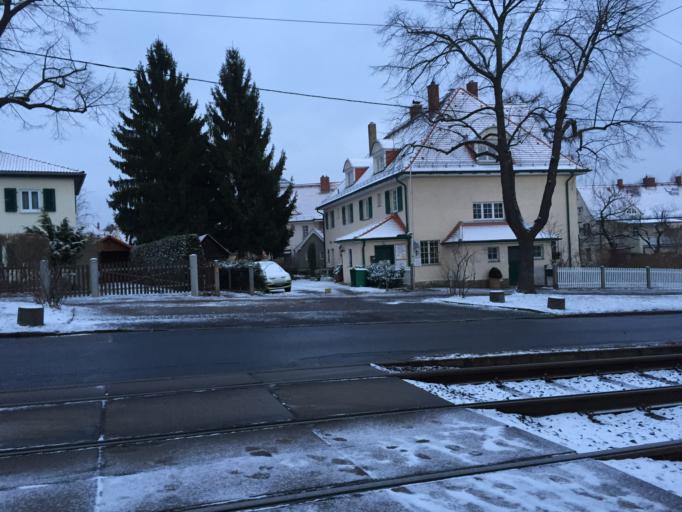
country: DE
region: Saxony
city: Albertstadt
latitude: 51.1117
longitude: 13.7624
